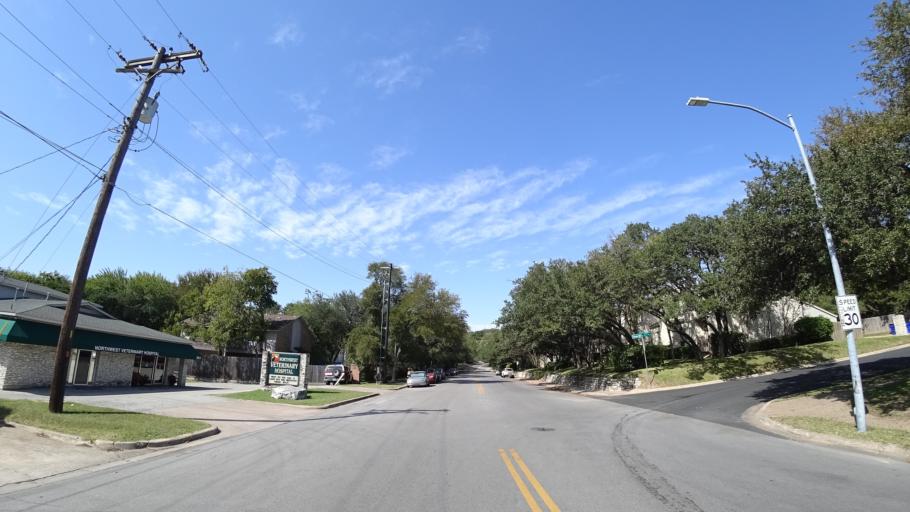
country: US
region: Texas
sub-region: Travis County
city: West Lake Hills
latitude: 30.3431
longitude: -97.7639
